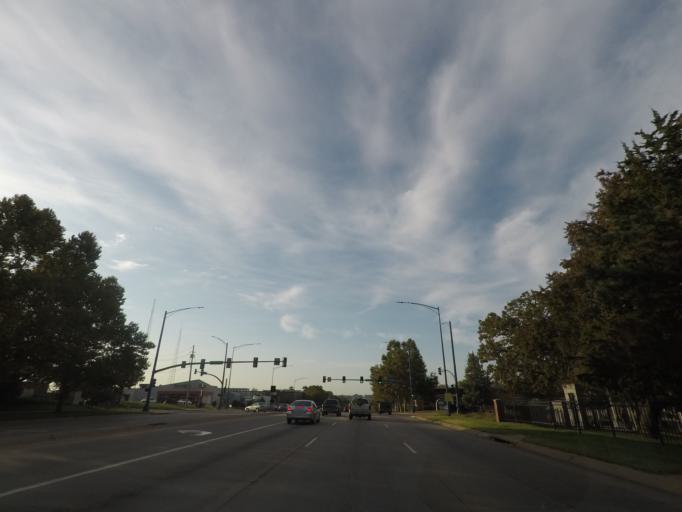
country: US
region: Iowa
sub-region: Polk County
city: Des Moines
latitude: 41.5887
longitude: -93.6449
